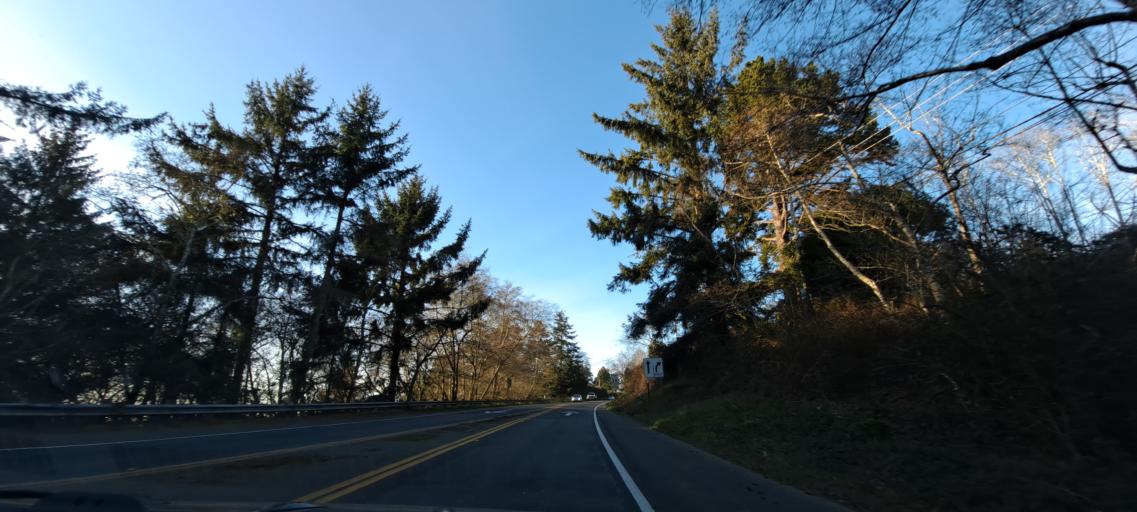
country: US
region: California
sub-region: Humboldt County
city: McKinleyville
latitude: 40.9236
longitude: -124.0996
